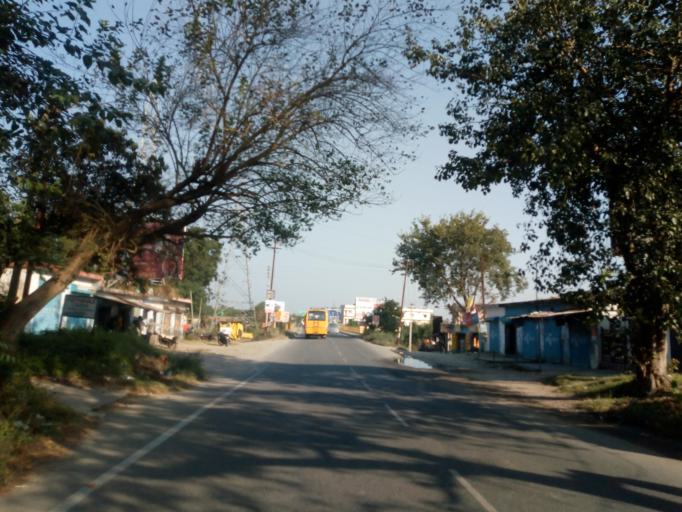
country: IN
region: Uttarakhand
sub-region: Dehradun
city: Dehradun
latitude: 30.3465
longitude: 77.8965
